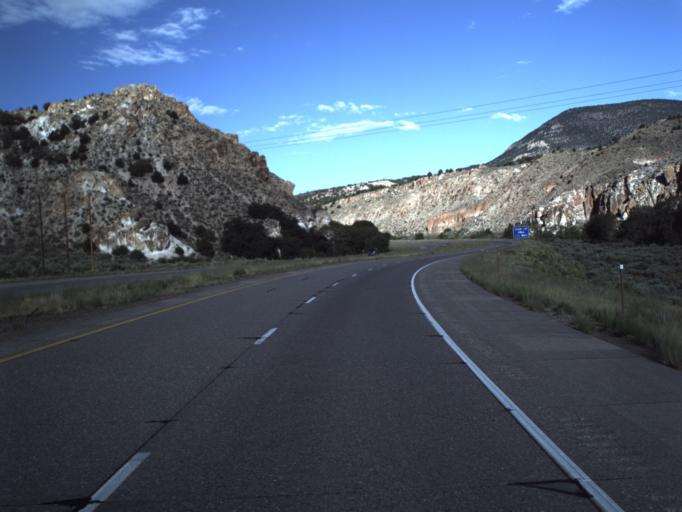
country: US
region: Utah
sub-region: Sevier County
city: Monroe
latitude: 38.5777
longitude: -112.3211
